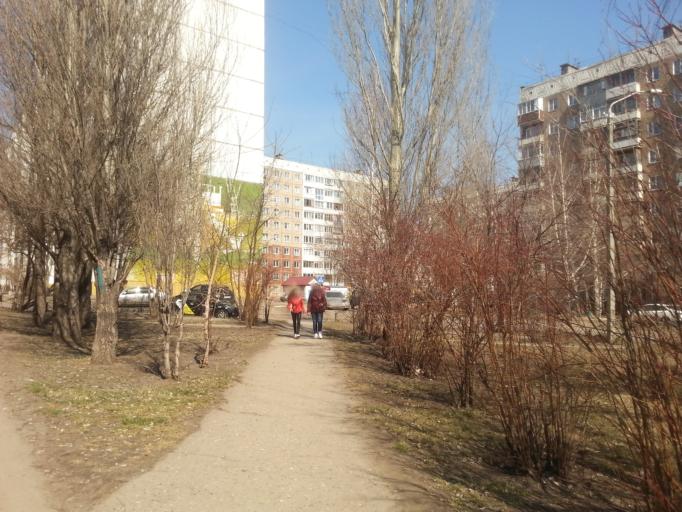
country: RU
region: Altai Krai
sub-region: Gorod Barnaulskiy
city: Barnaul
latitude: 53.3720
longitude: 83.6904
